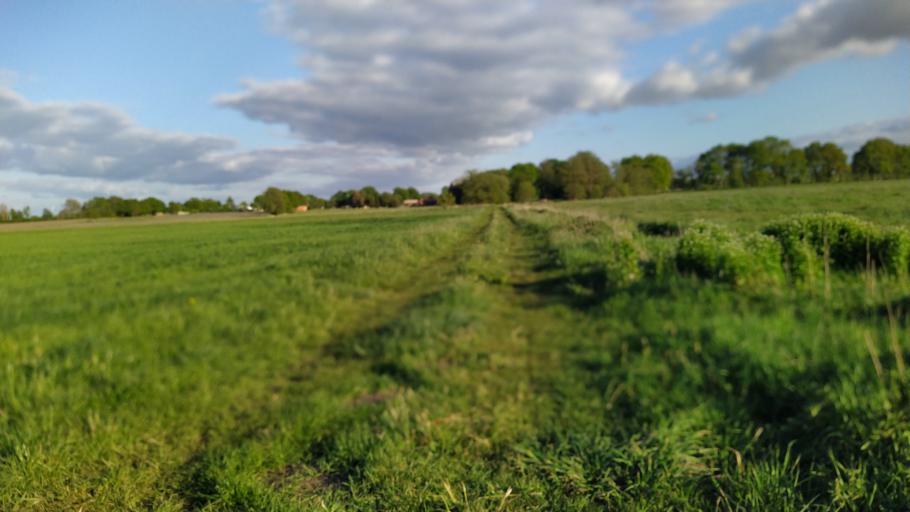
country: DE
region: Lower Saxony
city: Farven
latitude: 53.4470
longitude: 9.3370
